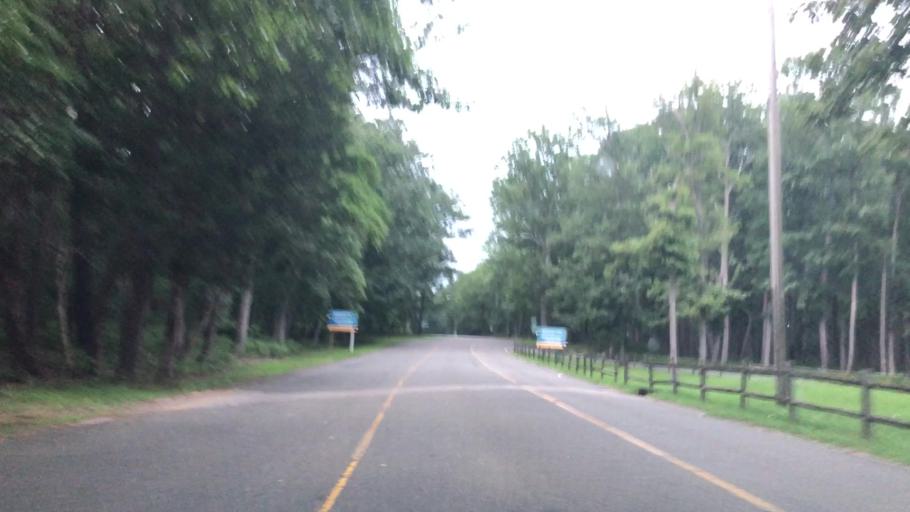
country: US
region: New Jersey
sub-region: Monmouth County
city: Shrewsbury
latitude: 40.1439
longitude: -74.4419
